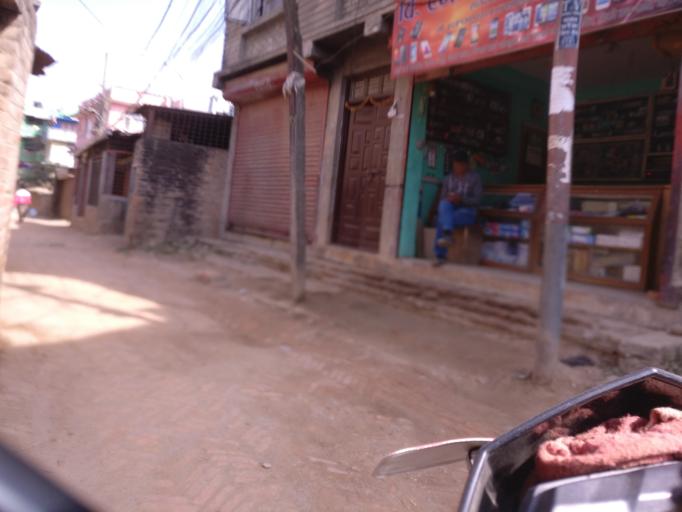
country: NP
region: Central Region
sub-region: Bagmati Zone
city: Patan
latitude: 27.6598
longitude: 85.3242
